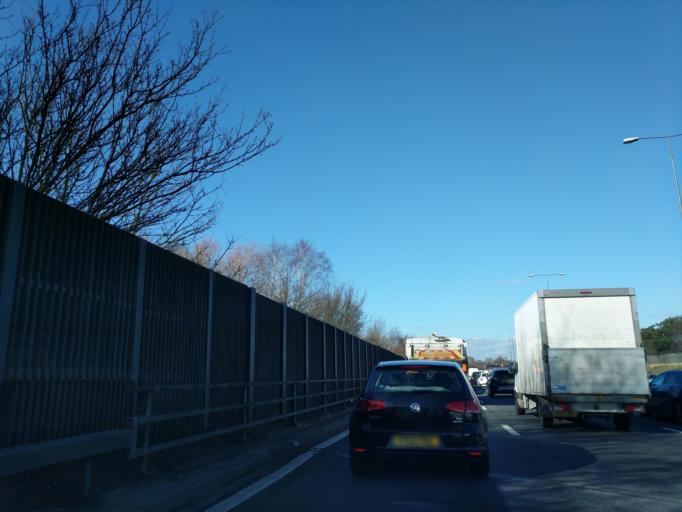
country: GB
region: England
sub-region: Surrey
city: Byfleet
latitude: 51.3289
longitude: -0.4781
